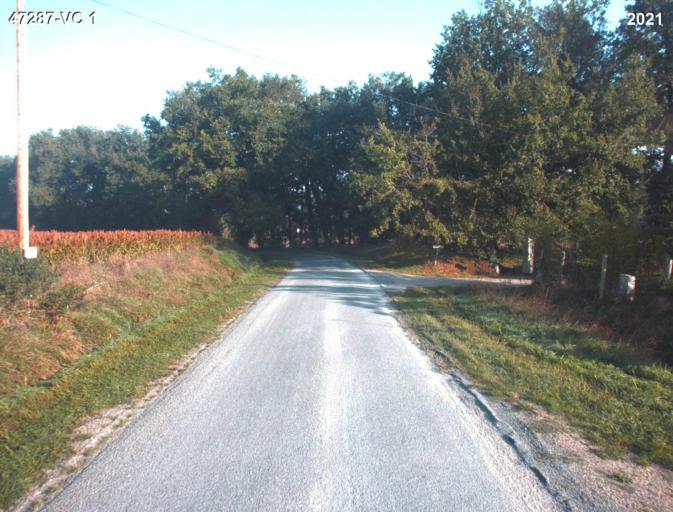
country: FR
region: Aquitaine
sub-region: Departement du Lot-et-Garonne
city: Sainte-Colombe-en-Bruilhois
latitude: 44.1389
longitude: 0.4468
